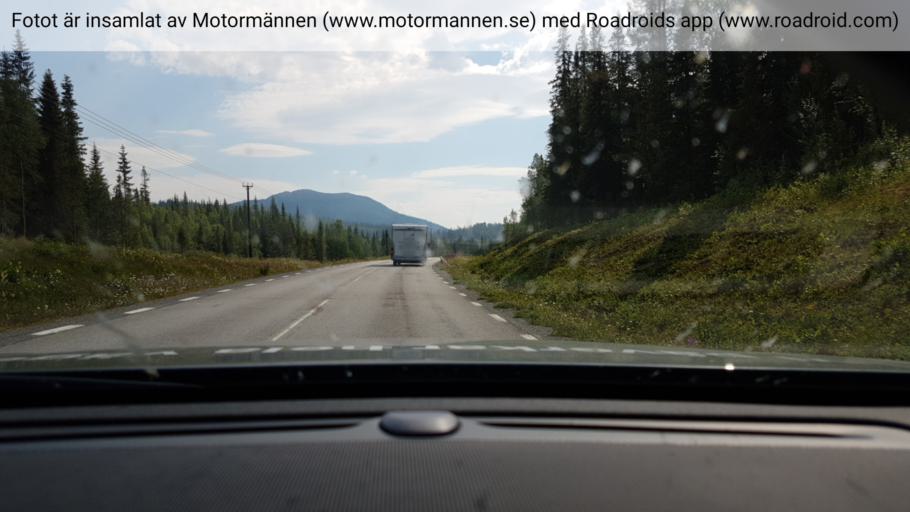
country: SE
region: Vaesterbotten
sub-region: Vilhelmina Kommun
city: Sjoberg
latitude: 65.5498
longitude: 15.5695
